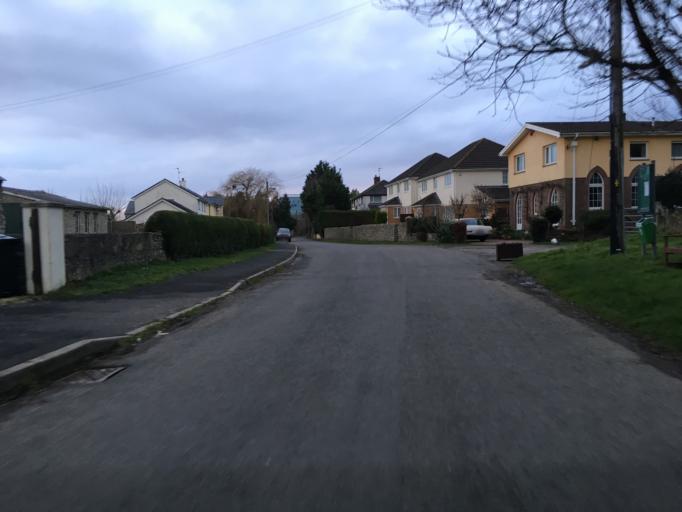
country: GB
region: Wales
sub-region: Newport
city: Bishton
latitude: 51.5846
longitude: -2.8787
